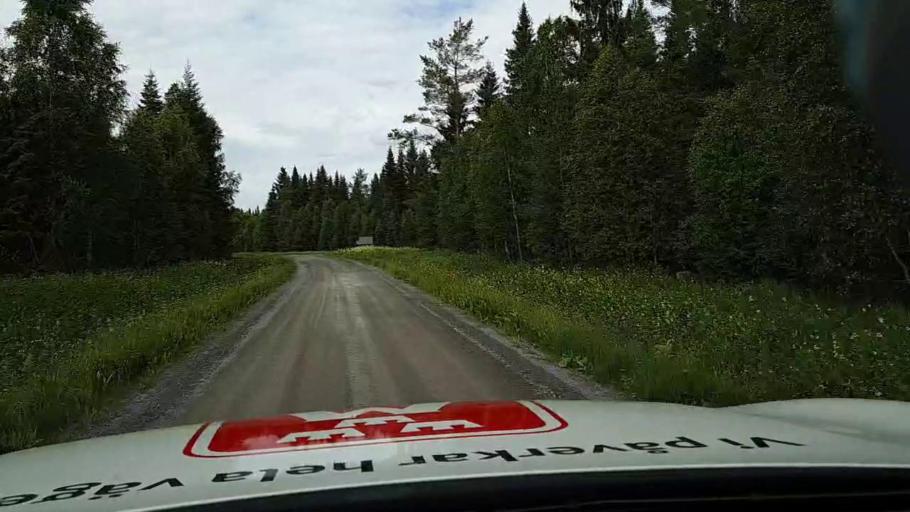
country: SE
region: Jaemtland
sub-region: OEstersunds Kommun
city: Lit
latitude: 63.3077
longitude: 15.2475
